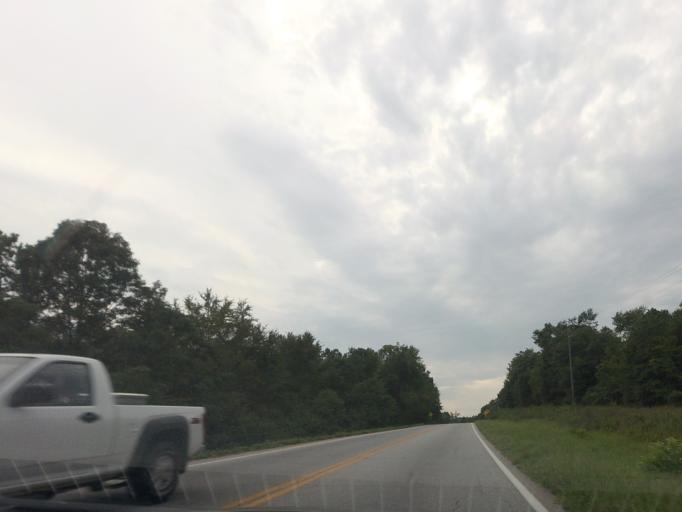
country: US
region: Georgia
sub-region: Twiggs County
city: Jeffersonville
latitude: 32.7645
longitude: -83.4689
